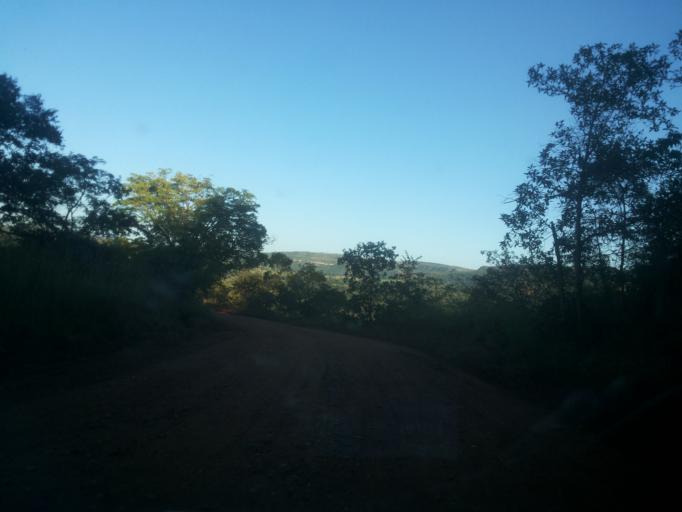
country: BR
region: Minas Gerais
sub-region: Campina Verde
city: Campina Verde
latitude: -19.3173
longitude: -49.8155
